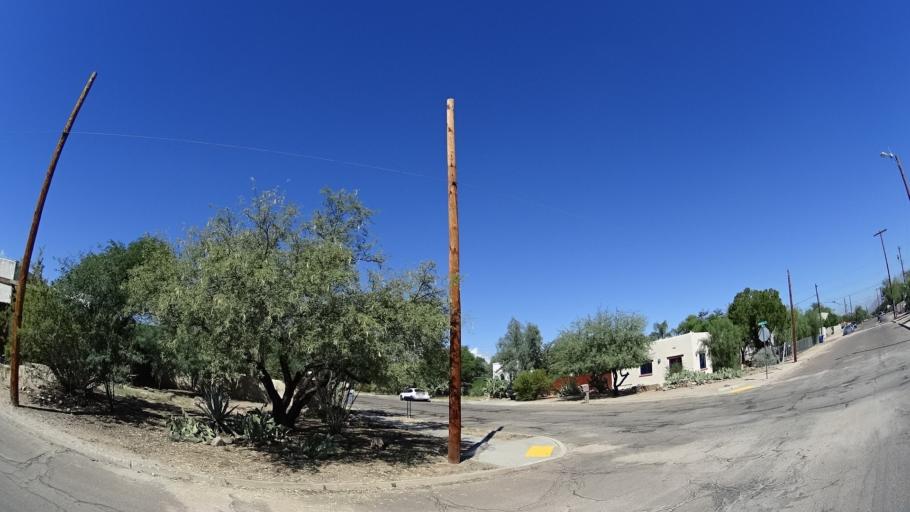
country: US
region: Arizona
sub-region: Pima County
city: Tucson
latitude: 32.2466
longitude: -110.9553
